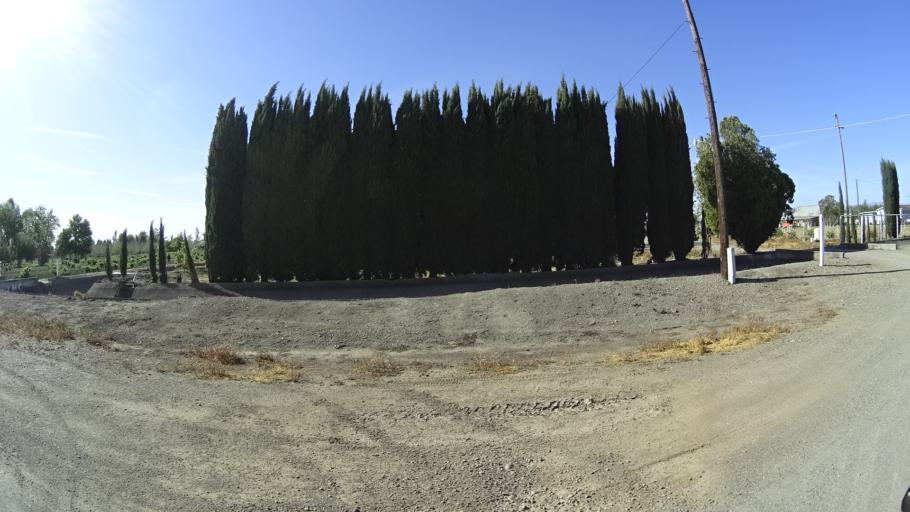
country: US
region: California
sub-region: Glenn County
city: Orland
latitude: 39.7222
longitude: -122.2027
